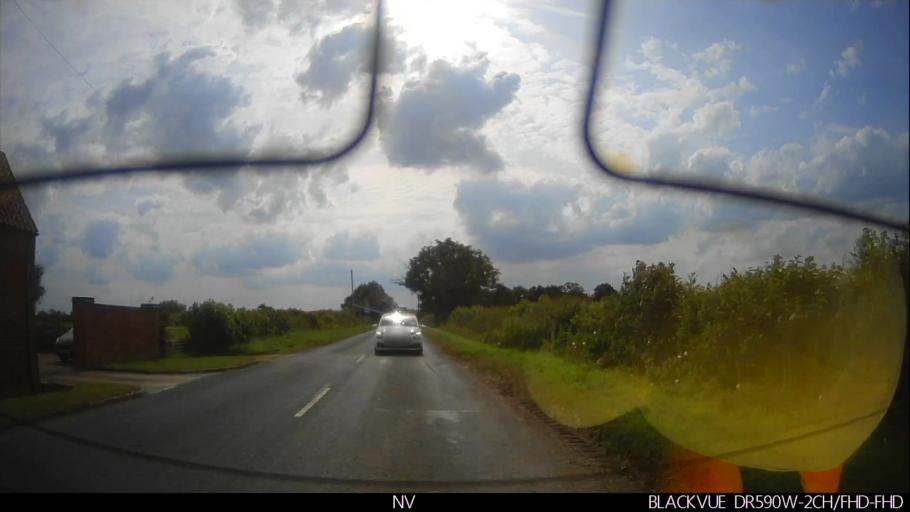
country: GB
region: England
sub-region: North Yorkshire
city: Marishes
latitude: 54.2069
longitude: -0.7921
